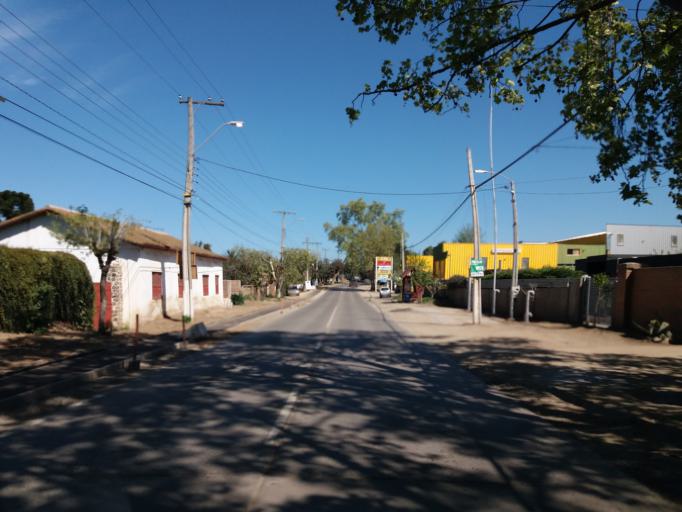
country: CL
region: Valparaiso
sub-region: Provincia de Marga Marga
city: Limache
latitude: -33.0006
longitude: -71.2086
